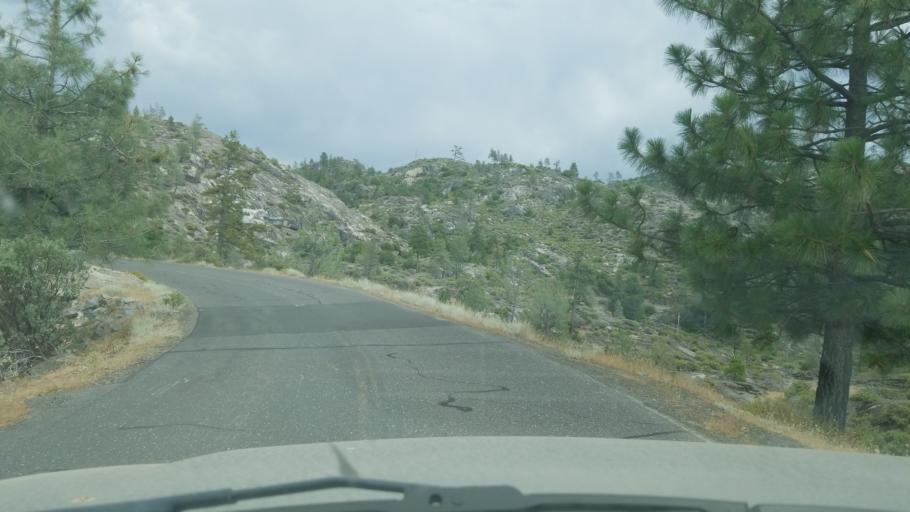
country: US
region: California
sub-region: Mariposa County
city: Yosemite Valley
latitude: 37.9011
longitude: -119.8393
